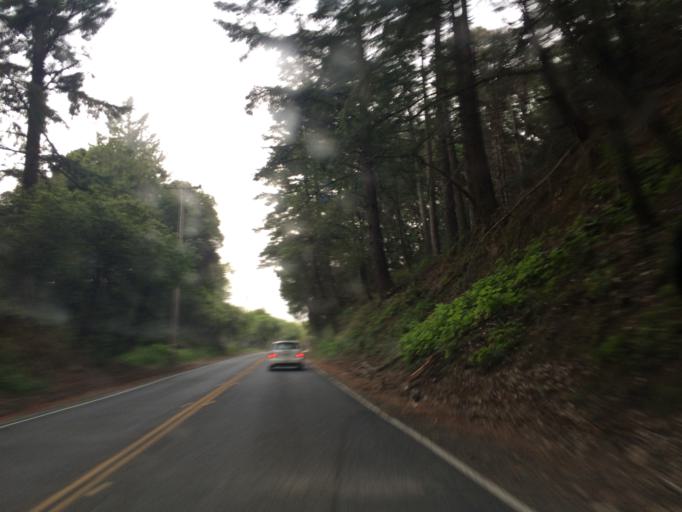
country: US
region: California
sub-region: Santa Clara County
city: Los Altos Hills
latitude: 37.3124
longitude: -122.1793
